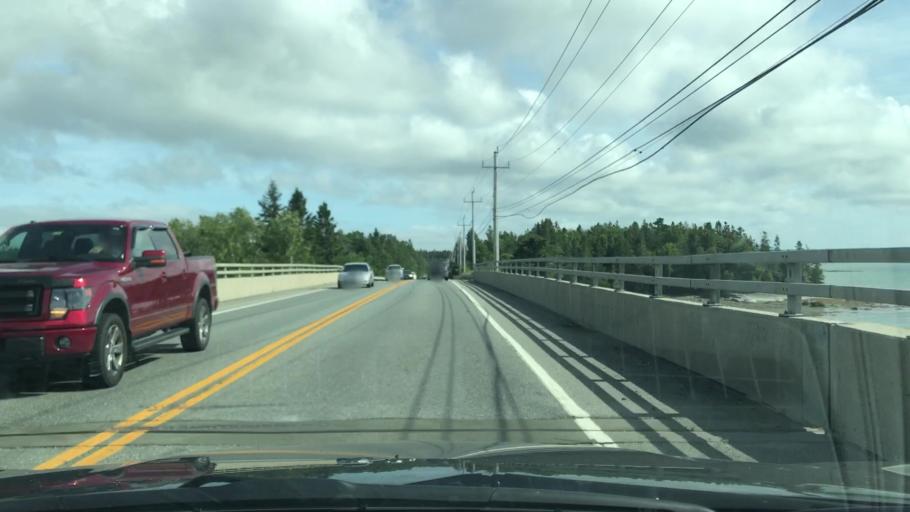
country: US
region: Maine
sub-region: Hancock County
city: Trenton
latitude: 44.4304
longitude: -68.3677
